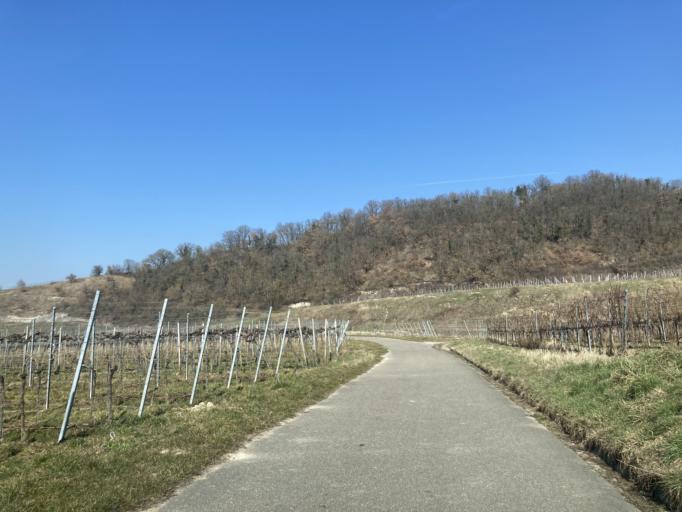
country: DE
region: Baden-Wuerttemberg
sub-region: Freiburg Region
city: Vogtsburg
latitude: 48.0711
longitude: 7.6396
